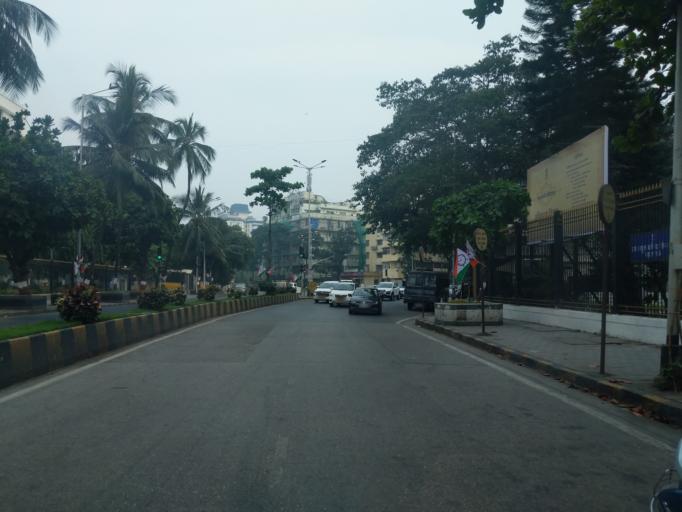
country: IN
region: Maharashtra
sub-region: Raigarh
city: Uran
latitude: 18.9269
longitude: 72.8264
